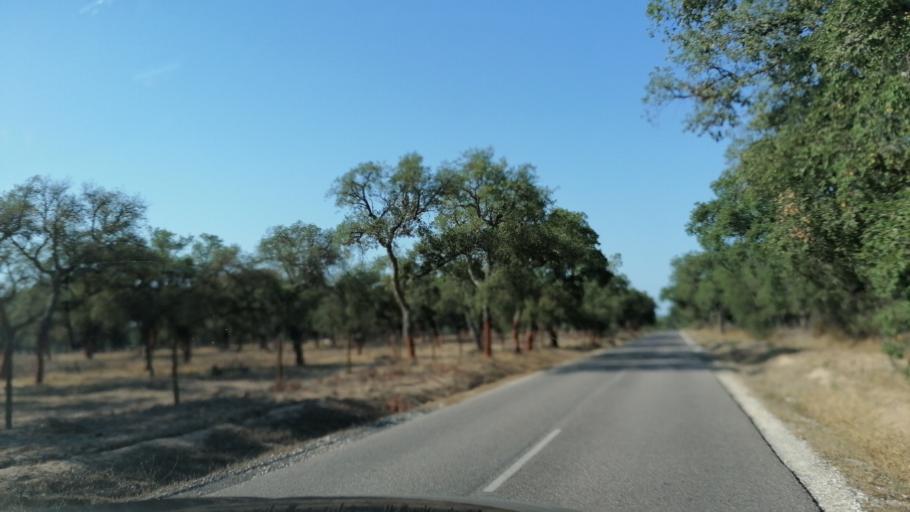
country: PT
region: Santarem
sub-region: Coruche
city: Coruche
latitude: 38.9215
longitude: -8.5237
